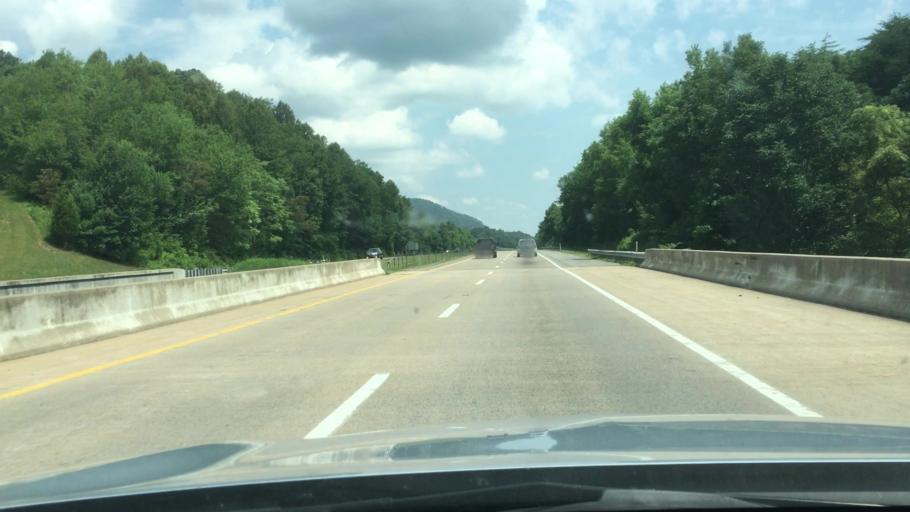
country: US
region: Tennessee
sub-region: Unicoi County
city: Unicoi
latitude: 36.2181
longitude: -82.3441
